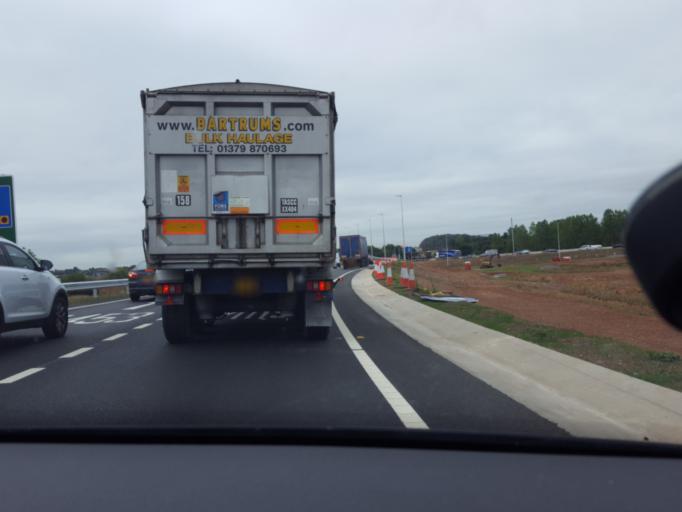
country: GB
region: England
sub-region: Leicestershire
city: Kegworth
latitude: 52.8535
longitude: -1.2949
